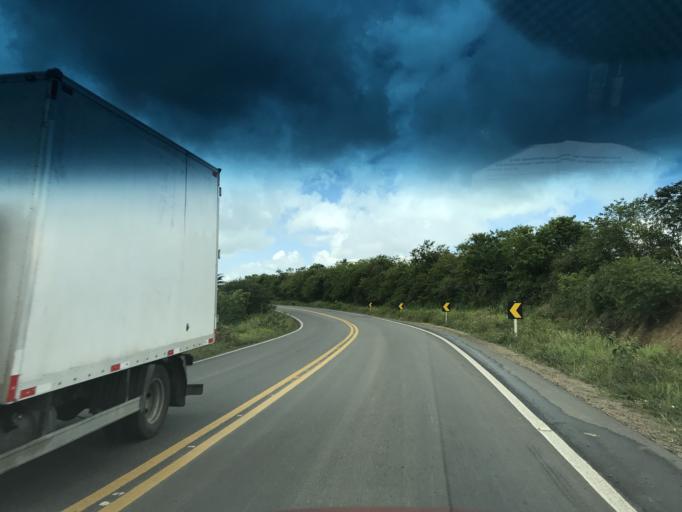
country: BR
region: Bahia
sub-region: Conceicao Do Almeida
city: Conceicao do Almeida
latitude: -12.7151
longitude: -39.2237
